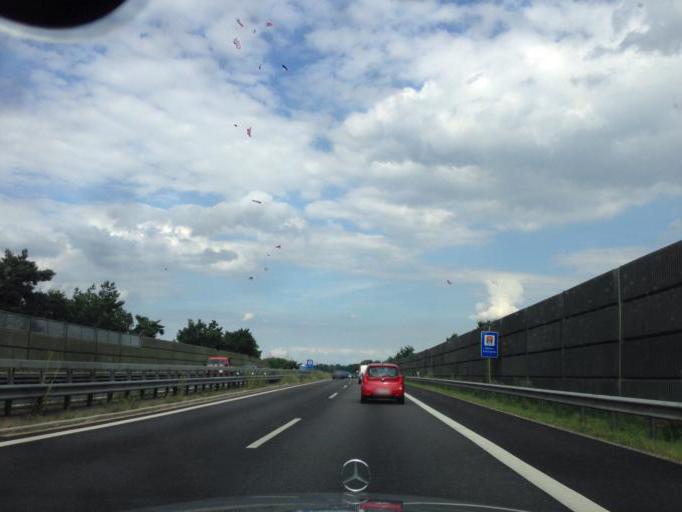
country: DE
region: Hamburg
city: Bergedorf
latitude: 53.4734
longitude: 10.1955
